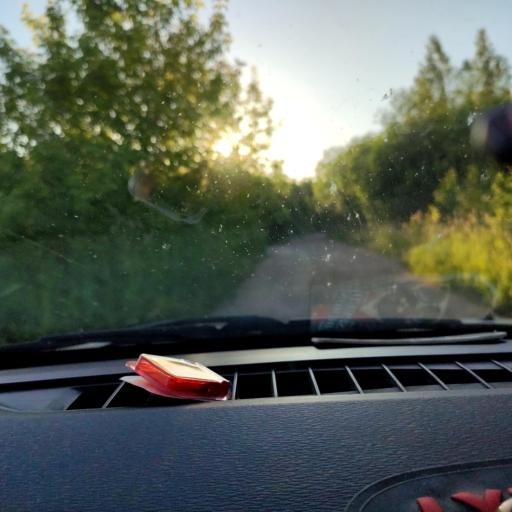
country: RU
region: Perm
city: Froly
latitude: 57.9450
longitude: 56.1977
